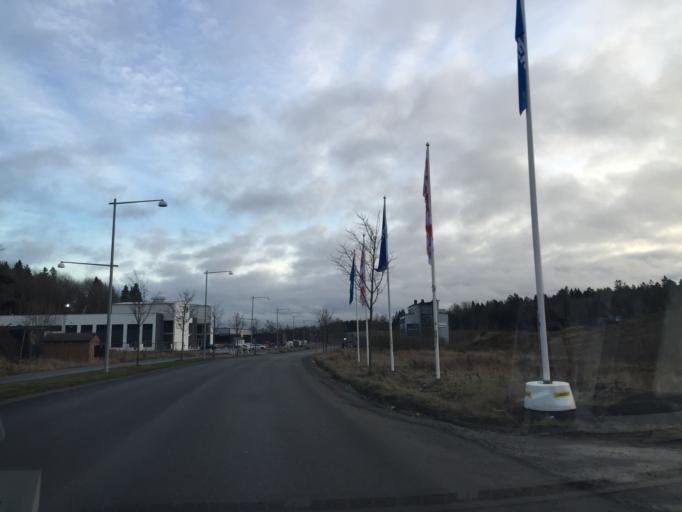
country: SE
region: Stockholm
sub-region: Sodertalje Kommun
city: Soedertaelje
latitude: 59.2012
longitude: 17.6698
